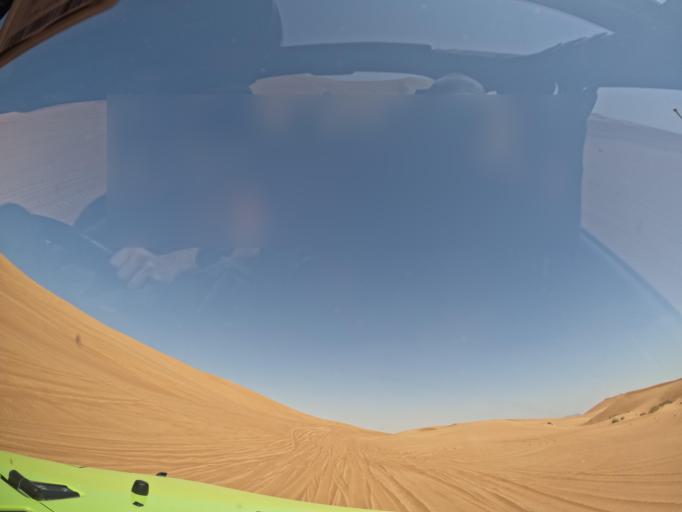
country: AE
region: Ash Shariqah
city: Adh Dhayd
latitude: 24.9857
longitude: 55.7239
